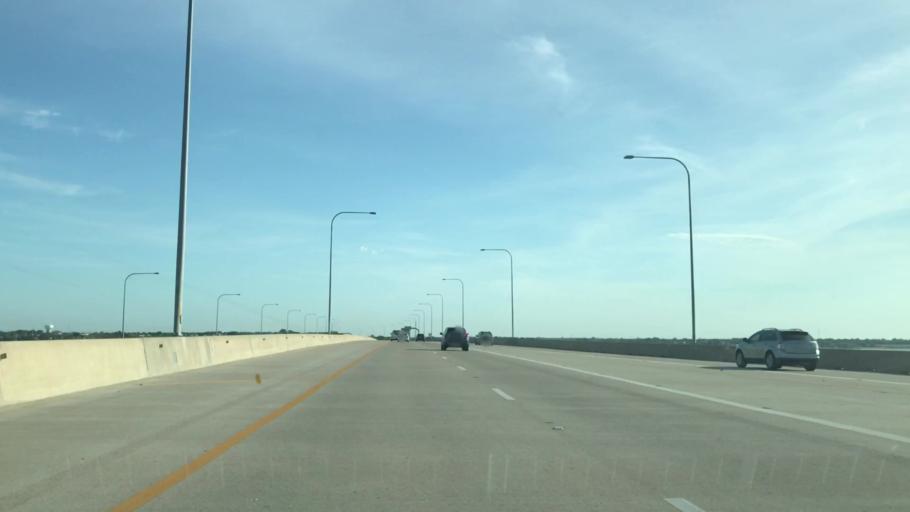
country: US
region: Texas
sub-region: Dallas County
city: Rowlett
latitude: 32.8647
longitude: -96.5542
